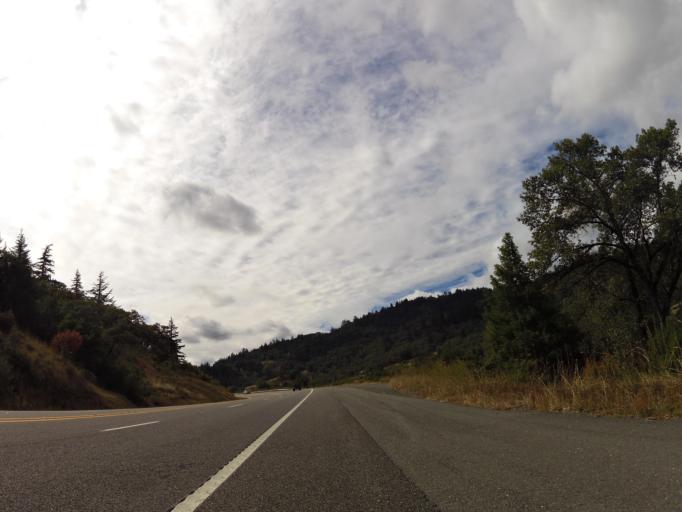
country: US
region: California
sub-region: Humboldt County
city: Redway
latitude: 40.1627
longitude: -123.7891
